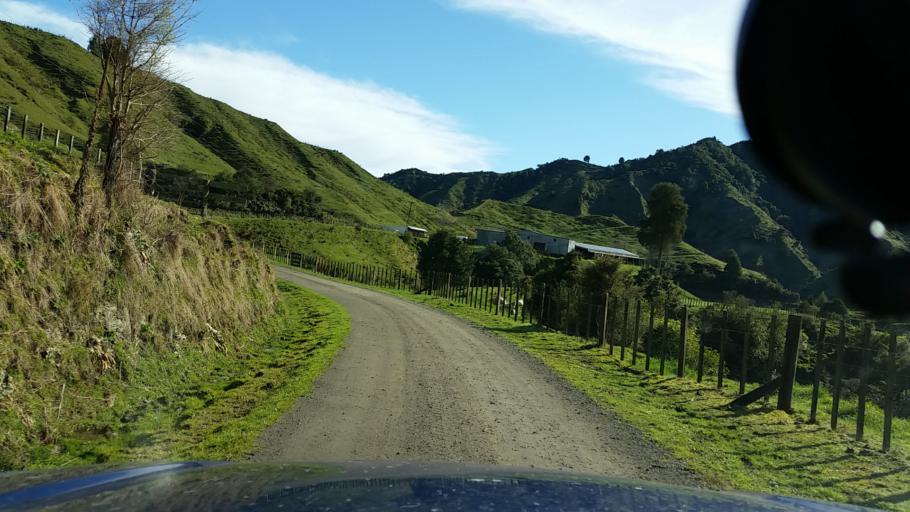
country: NZ
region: Taranaki
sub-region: New Plymouth District
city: Waitara
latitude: -39.0523
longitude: 174.7494
